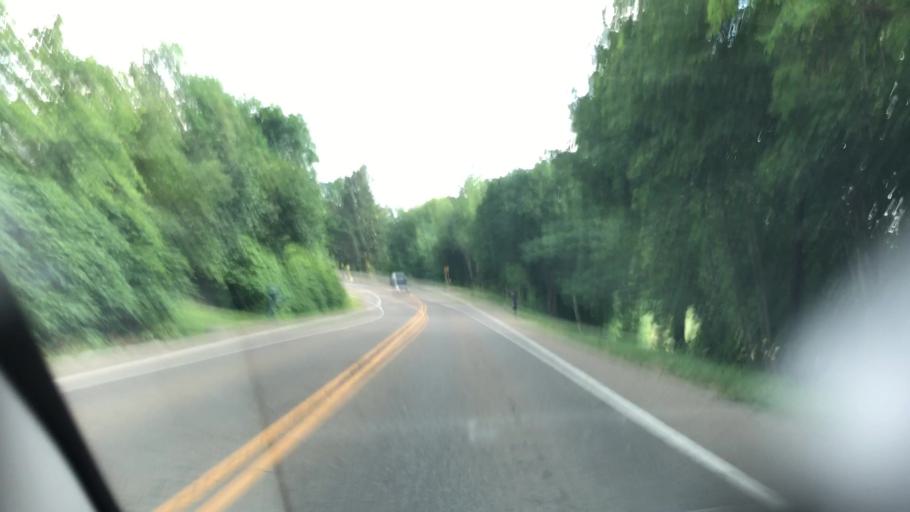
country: US
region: Ohio
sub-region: Summit County
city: Fairlawn
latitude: 41.0849
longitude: -81.6446
